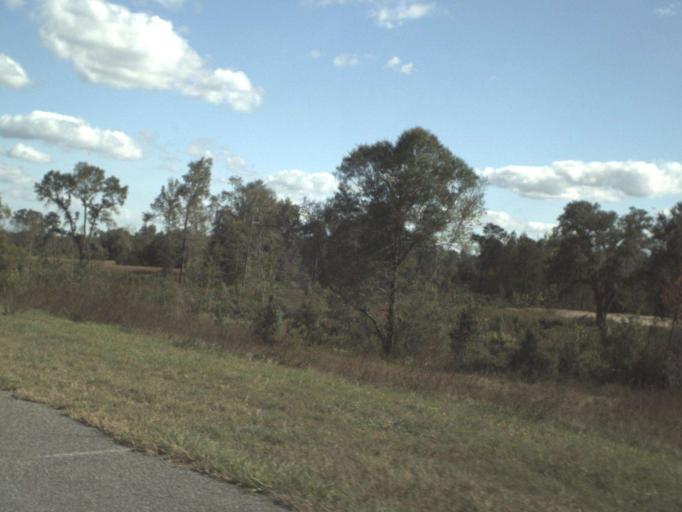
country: US
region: Florida
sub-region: Holmes County
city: Bonifay
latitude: 30.7727
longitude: -85.8205
